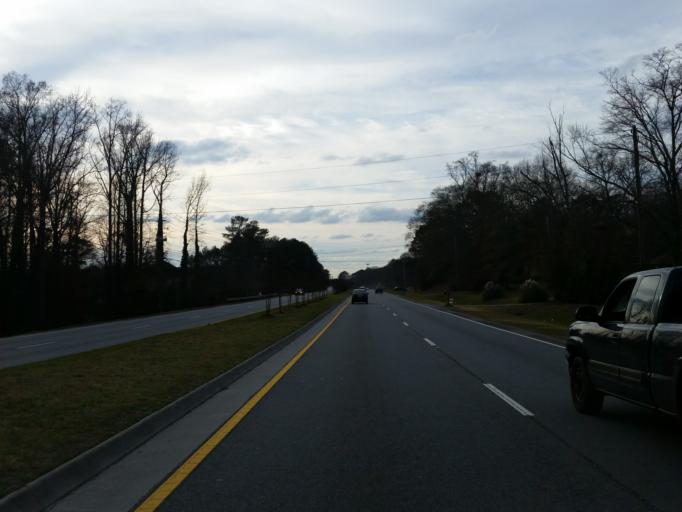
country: US
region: Georgia
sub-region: Cobb County
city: Fair Oaks
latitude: 33.9038
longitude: -84.6135
